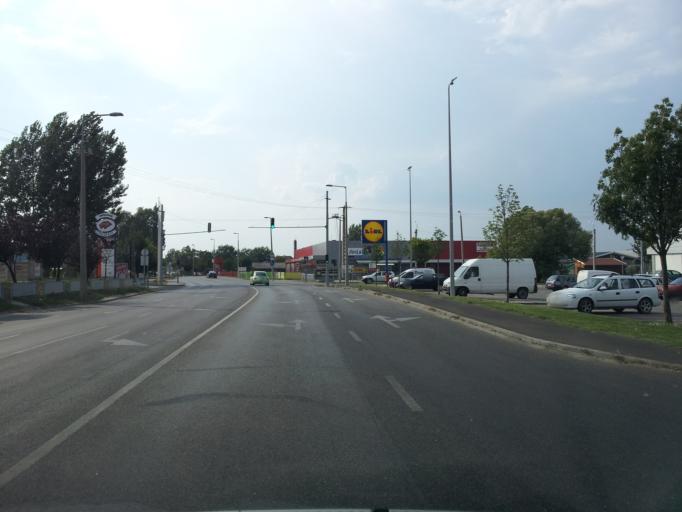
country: HU
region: Pest
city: Dunaharaszti
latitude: 47.3463
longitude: 19.1172
